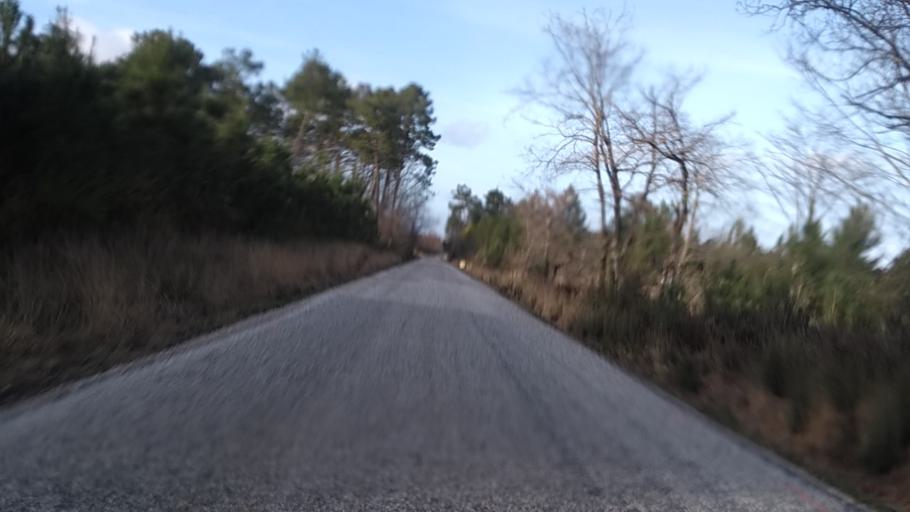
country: FR
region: Aquitaine
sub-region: Departement de la Gironde
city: Le Barp
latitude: 44.5876
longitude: -0.7694
